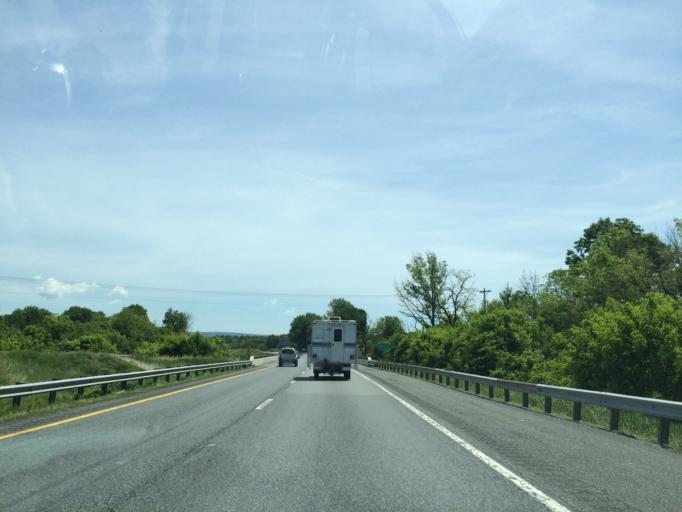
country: US
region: Maryland
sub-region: Washington County
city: Hagerstown
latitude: 39.5997
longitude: -77.7035
